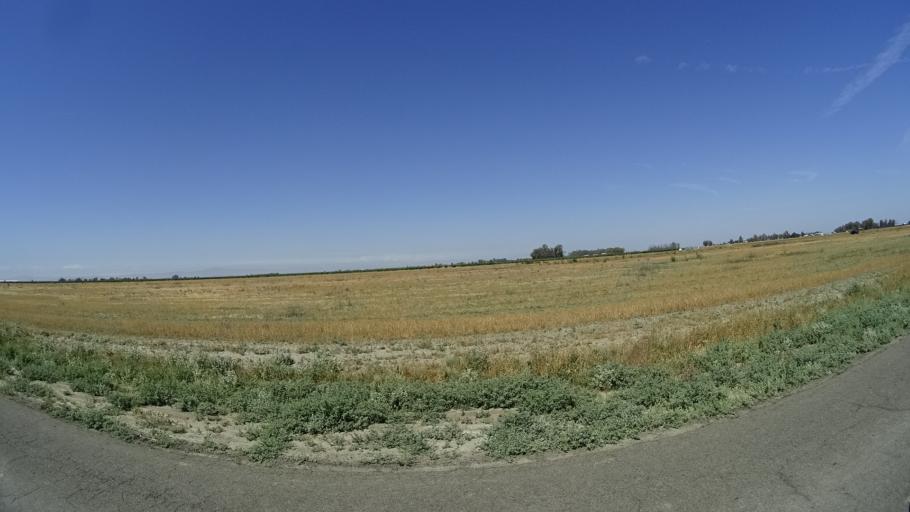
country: US
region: California
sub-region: Kings County
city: Stratford
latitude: 36.1875
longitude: -119.7803
